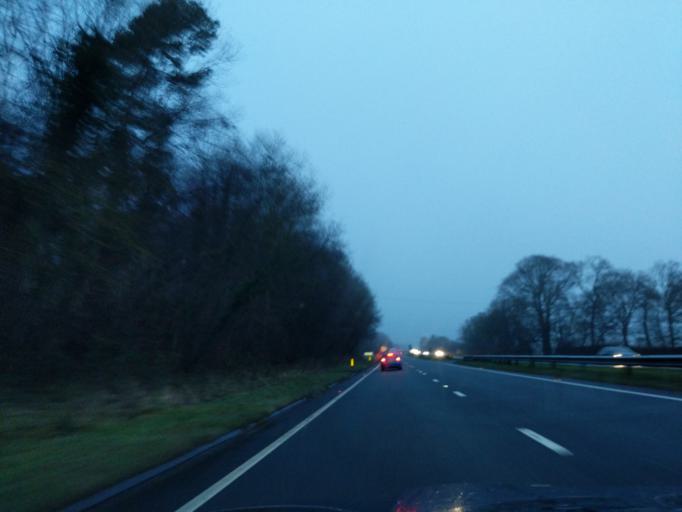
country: GB
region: England
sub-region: Northumberland
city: Felton
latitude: 55.3365
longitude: -1.7260
